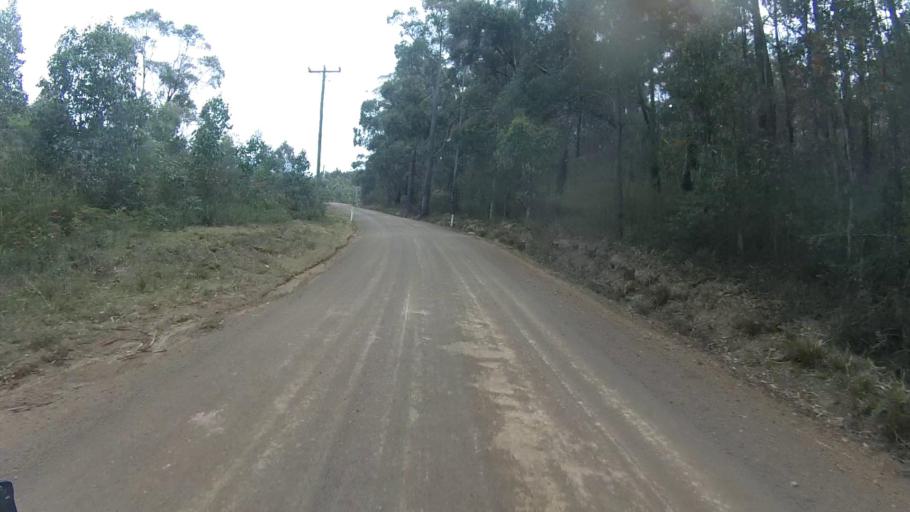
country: AU
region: Tasmania
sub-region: Sorell
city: Sorell
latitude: -42.7614
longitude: 147.8024
